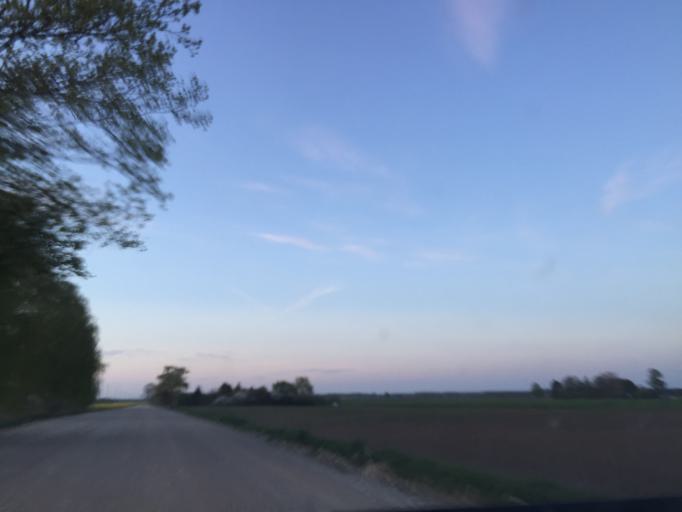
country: LV
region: Rundales
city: Pilsrundale
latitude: 56.4553
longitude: 24.0668
